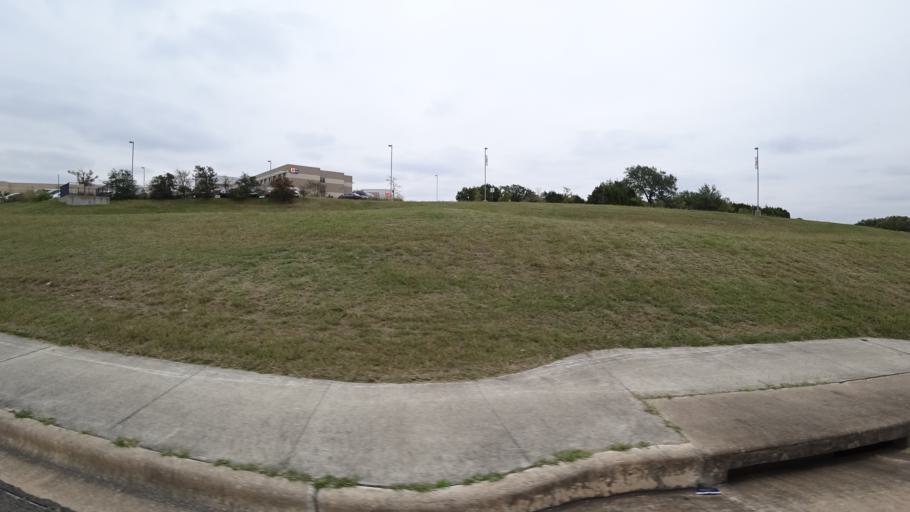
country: US
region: Texas
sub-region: Travis County
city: Shady Hollow
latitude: 30.2129
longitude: -97.8929
